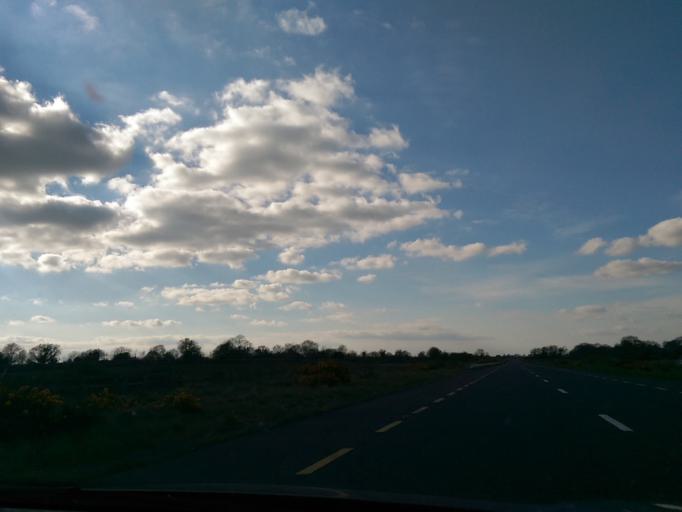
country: IE
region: Connaught
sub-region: County Galway
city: Loughrea
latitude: 53.2212
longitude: -8.5824
